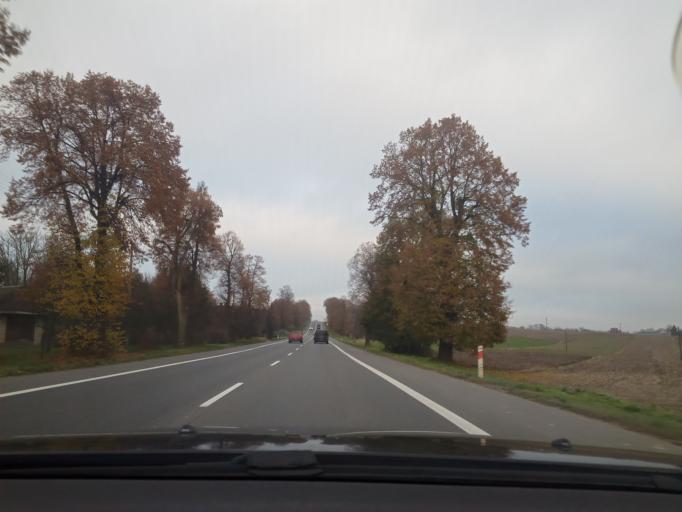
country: PL
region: Lesser Poland Voivodeship
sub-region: Powiat miechowski
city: Miechow
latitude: 50.3390
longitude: 20.0345
